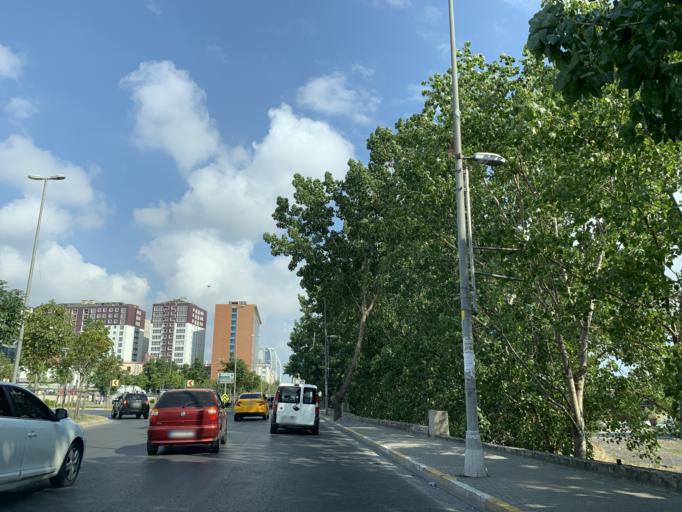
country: TR
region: Istanbul
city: Esenyurt
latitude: 41.0276
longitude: 28.6667
